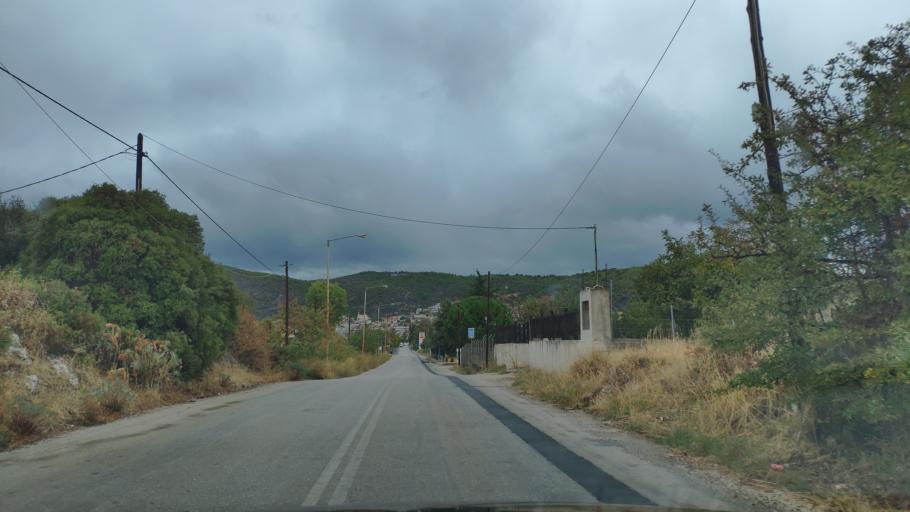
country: GR
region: Peloponnese
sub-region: Nomos Korinthias
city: Perachora
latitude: 38.0207
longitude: 22.9476
